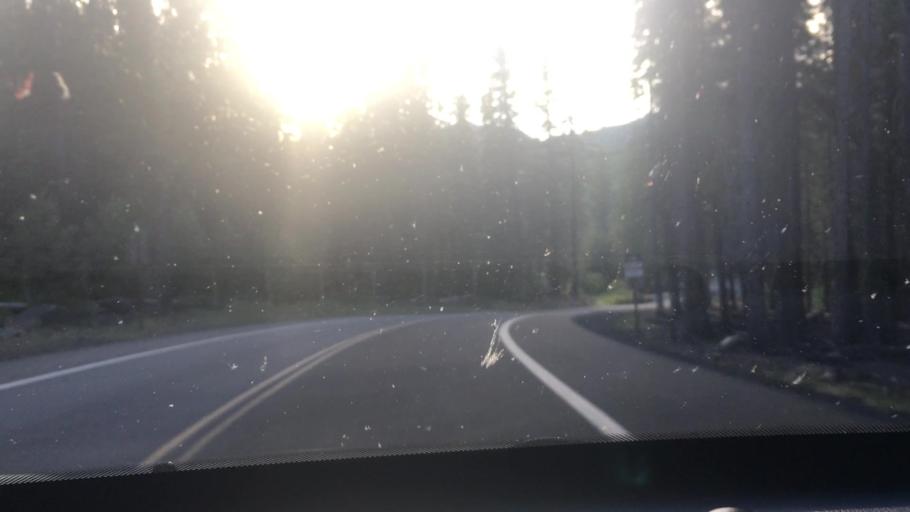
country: US
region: Oregon
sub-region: Deschutes County
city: Deschutes River Woods
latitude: 44.0312
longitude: -121.5195
